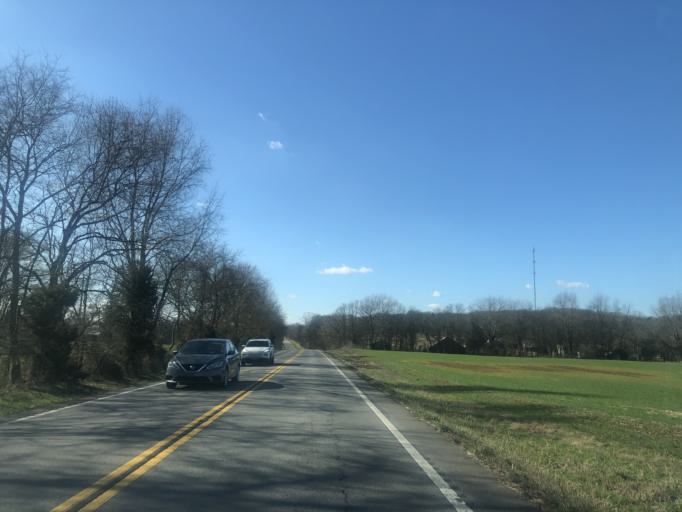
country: US
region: Tennessee
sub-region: Williamson County
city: Nolensville
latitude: 35.8525
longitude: -86.6381
